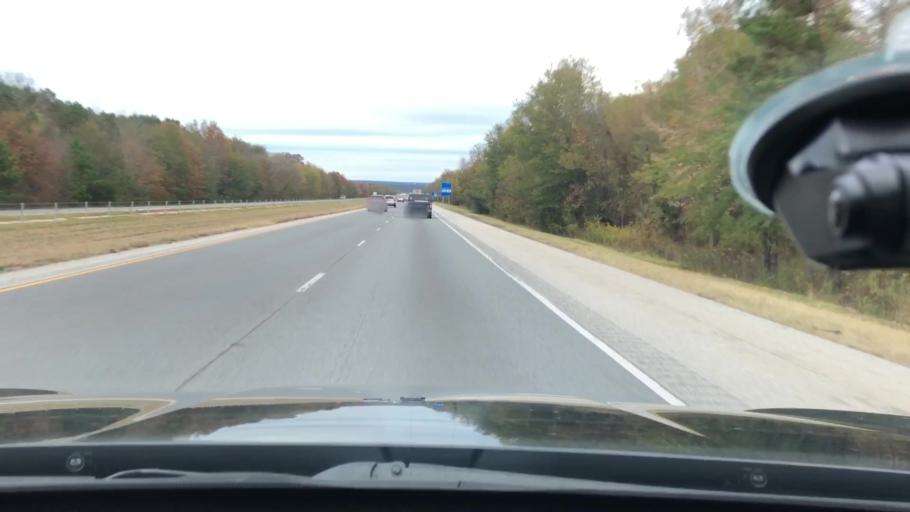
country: US
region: Arkansas
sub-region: Clark County
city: Arkadelphia
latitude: 34.1541
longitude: -93.0779
